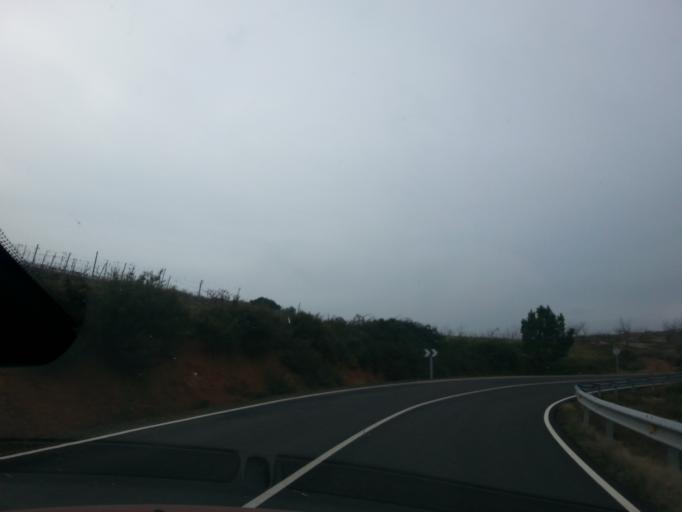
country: ES
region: Castille and Leon
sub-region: Provincia de Salamanca
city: Sotoserrano
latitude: 40.4370
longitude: -6.0431
